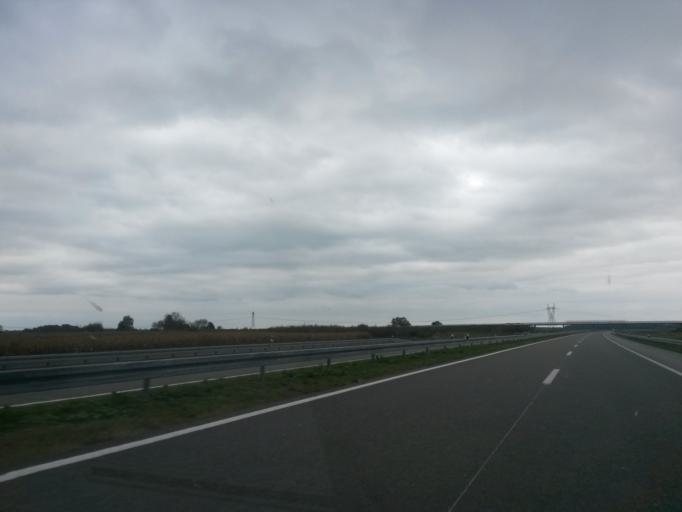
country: HR
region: Osjecko-Baranjska
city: Vuka
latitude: 45.4405
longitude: 18.4610
